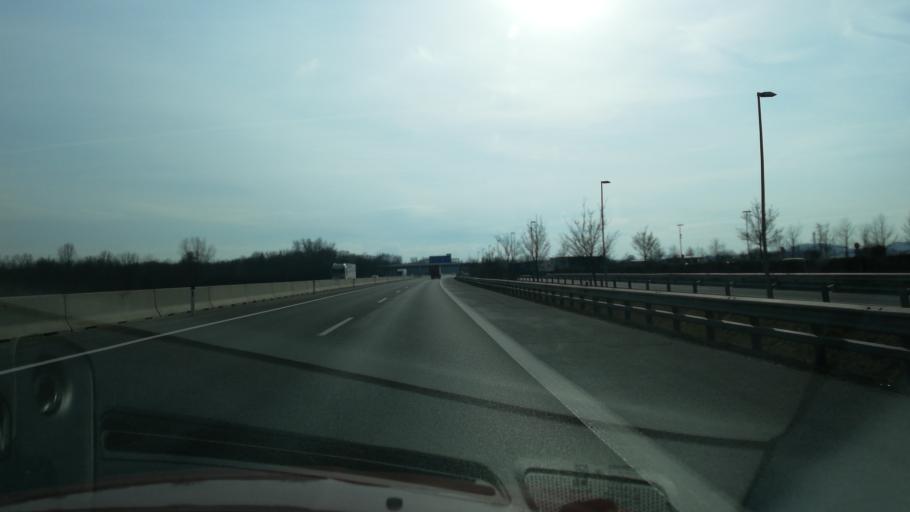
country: AT
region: Lower Austria
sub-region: Politischer Bezirk Sankt Polten
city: Herzogenburg
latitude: 48.3111
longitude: 15.7153
